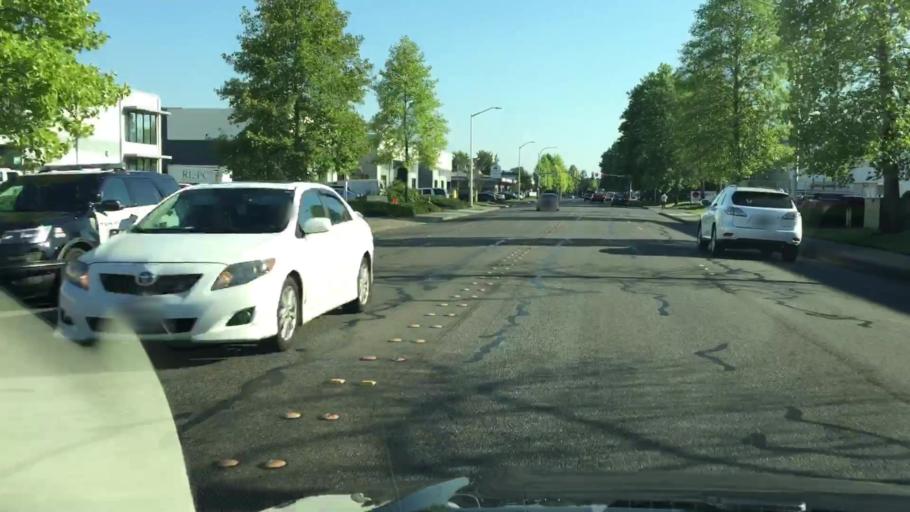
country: US
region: Washington
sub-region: King County
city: Tukwila
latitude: 47.4505
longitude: -122.2508
